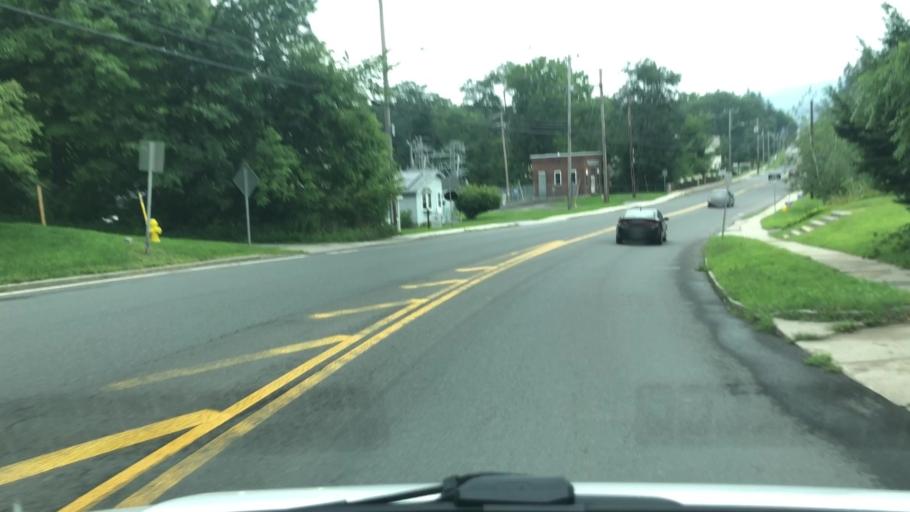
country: US
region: Massachusetts
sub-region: Berkshire County
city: Williamstown
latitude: 42.7106
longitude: -73.1962
